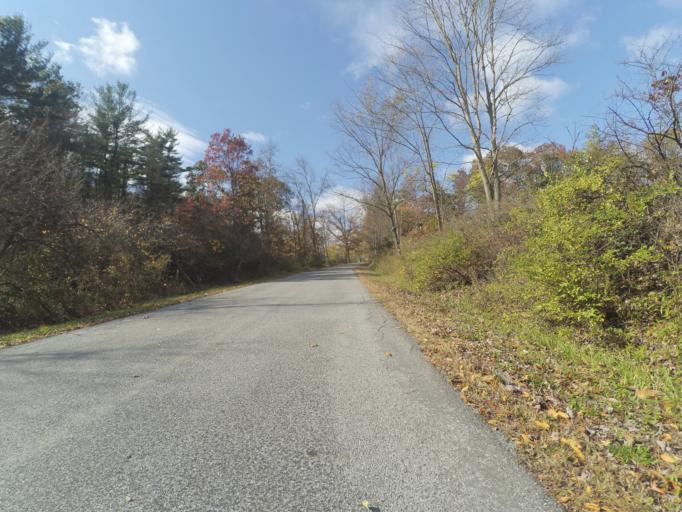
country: US
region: Pennsylvania
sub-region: Centre County
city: Park Forest Village
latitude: 40.8615
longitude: -77.9672
